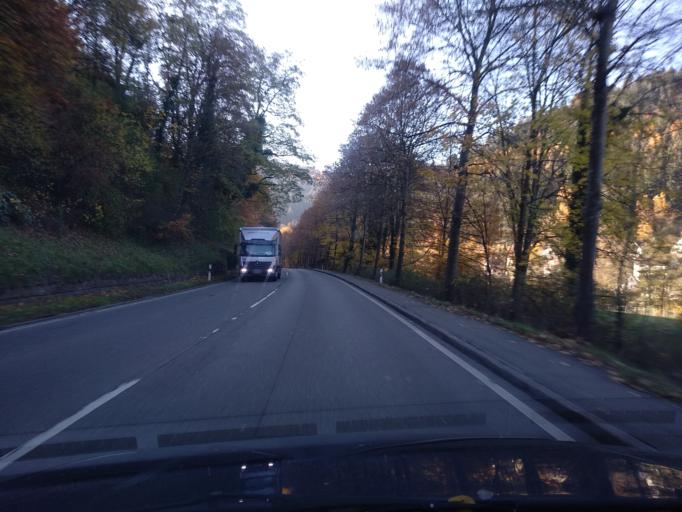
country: DE
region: Baden-Wuerttemberg
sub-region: Karlsruhe Region
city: Calw
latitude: 48.7323
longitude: 8.7349
